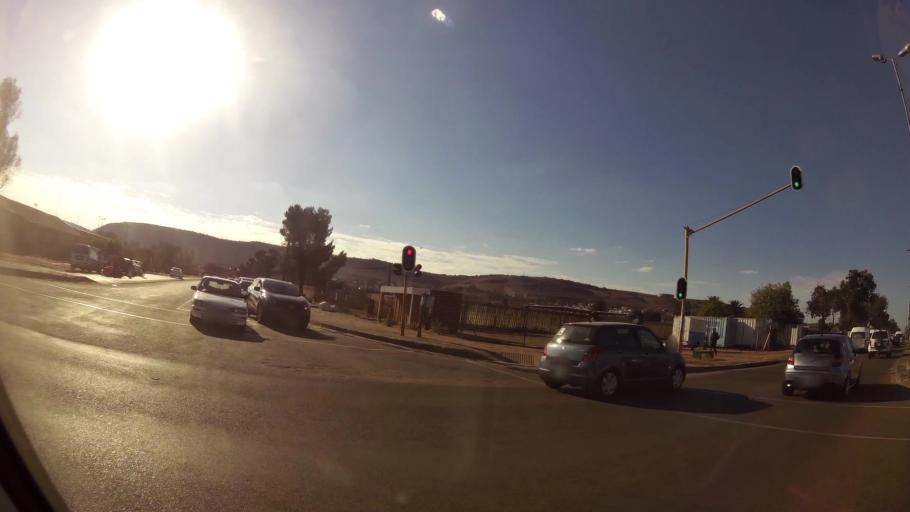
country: ZA
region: Gauteng
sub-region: City of Tshwane Metropolitan Municipality
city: Cullinan
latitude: -25.7121
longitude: 28.3787
